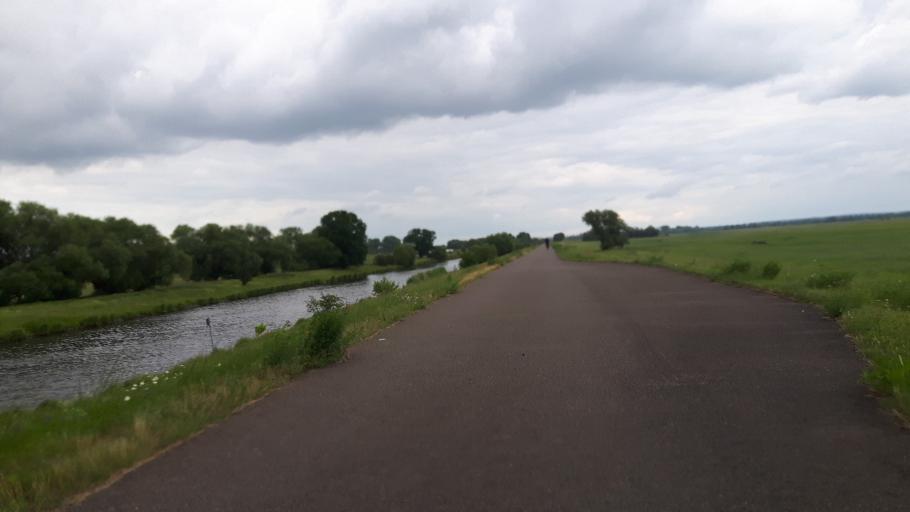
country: DE
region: Brandenburg
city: Meyenburg
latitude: 53.0264
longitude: 14.2478
